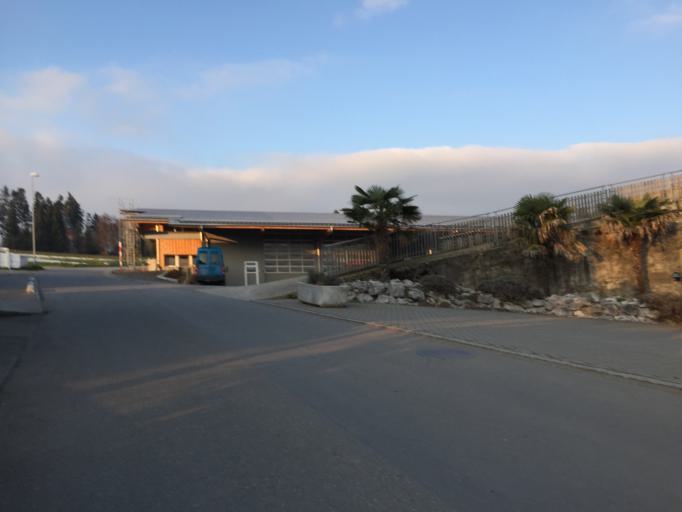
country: CH
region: Bern
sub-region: Bern-Mittelland District
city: Taegertschi
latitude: 46.8802
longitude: 7.5799
